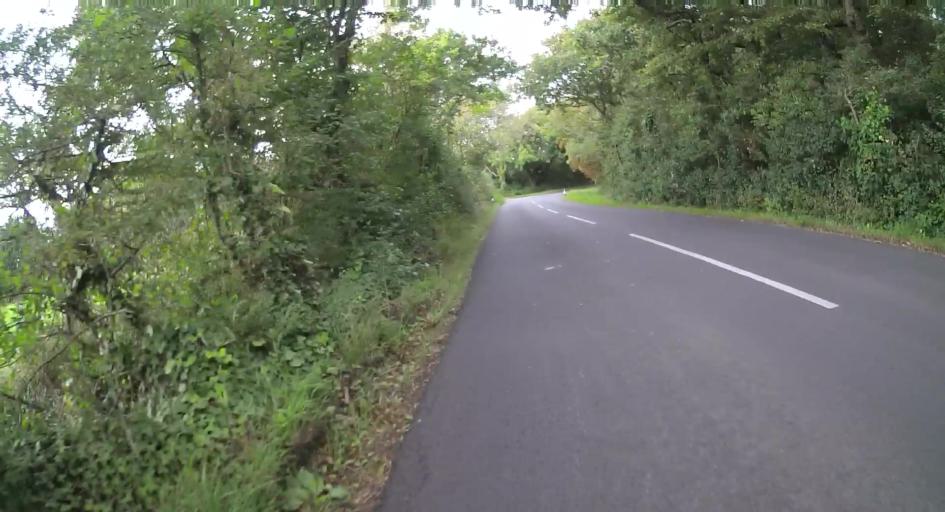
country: GB
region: England
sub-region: Isle of Wight
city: Freshwater
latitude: 50.6813
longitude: -1.4959
